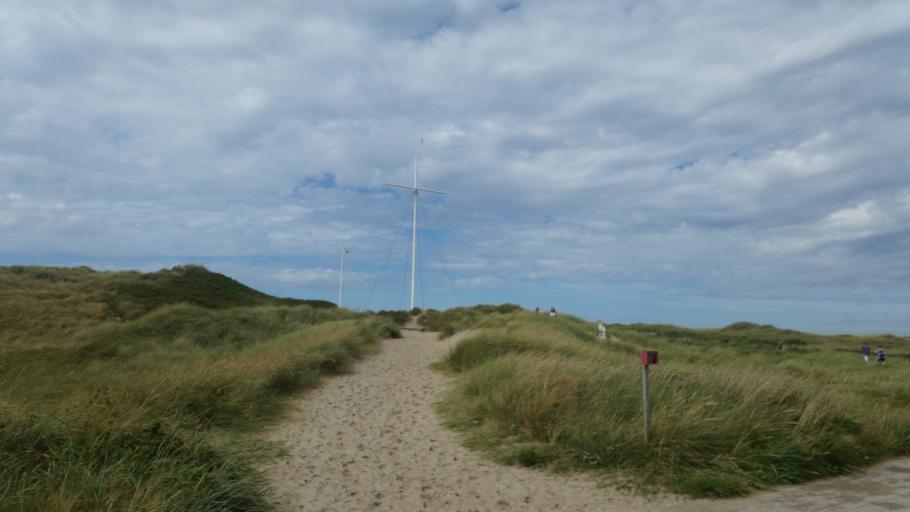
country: DK
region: Central Jutland
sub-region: Lemvig Kommune
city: Thyboron
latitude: 56.7829
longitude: 8.2318
